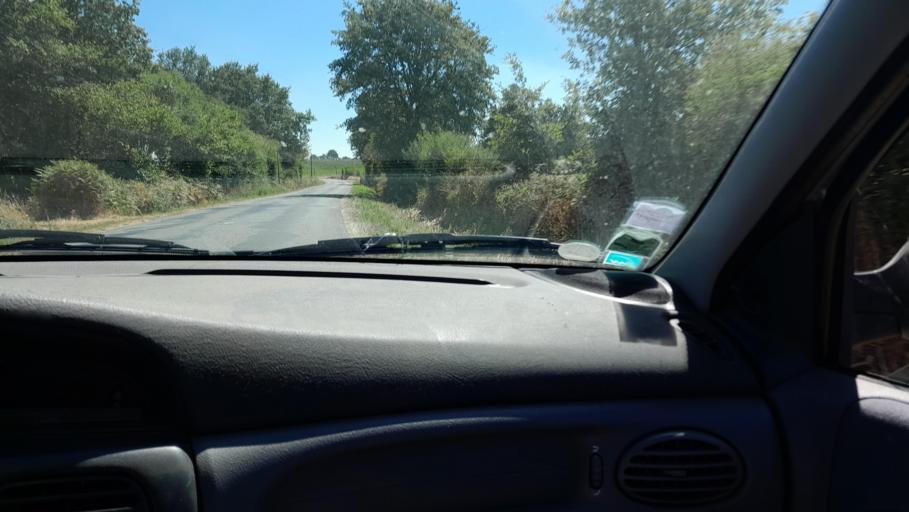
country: FR
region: Pays de la Loire
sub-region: Departement de Maine-et-Loire
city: Pouance
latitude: 47.7762
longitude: -1.1933
